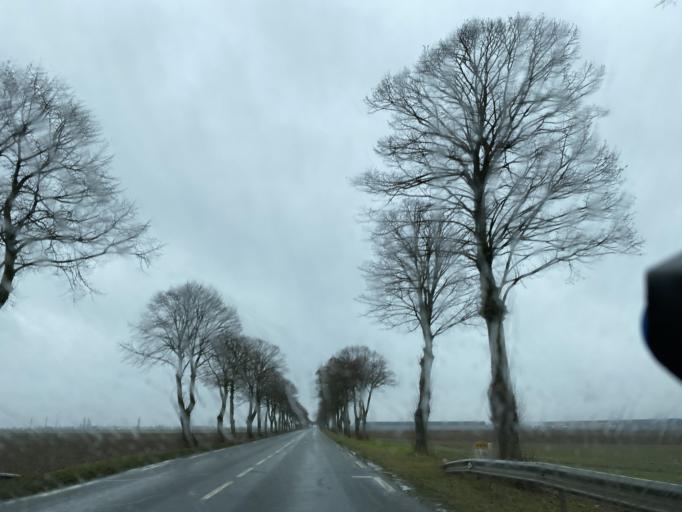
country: FR
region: Centre
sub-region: Departement du Loiret
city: Artenay
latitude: 48.1033
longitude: 1.8644
